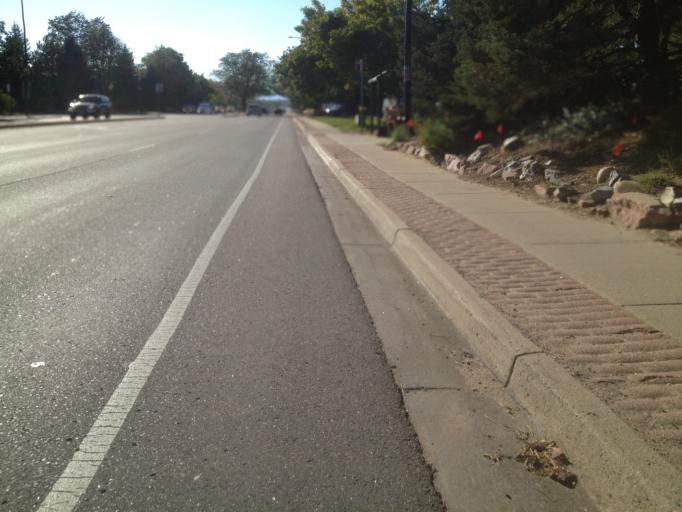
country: US
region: Colorado
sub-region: Boulder County
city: Louisville
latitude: 39.9870
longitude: -105.1139
